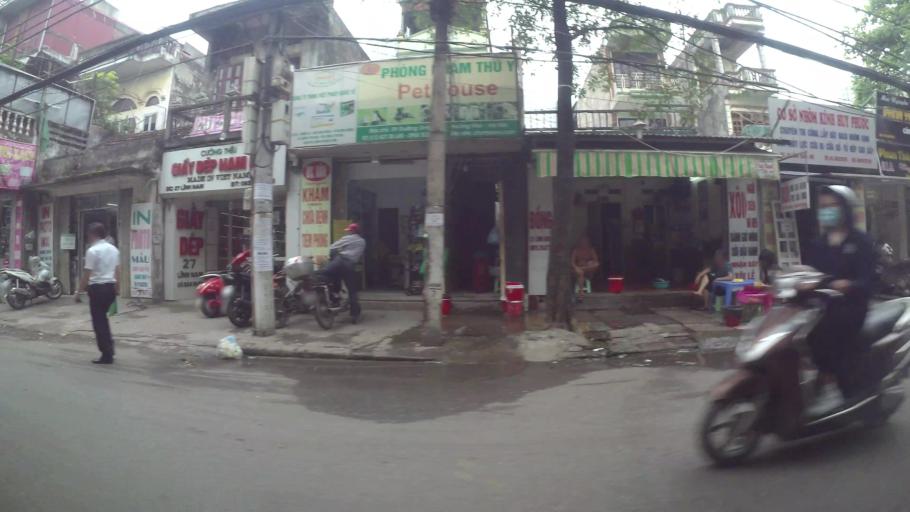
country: VN
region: Ha Noi
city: Hai BaTrung
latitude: 20.9905
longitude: 105.8645
